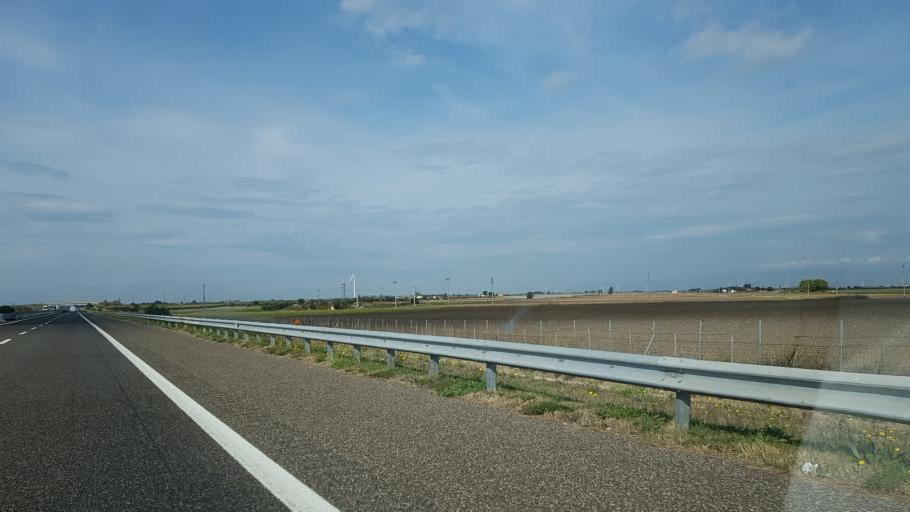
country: IT
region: Apulia
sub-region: Provincia di Foggia
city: Stornara
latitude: 41.3640
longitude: 15.7878
